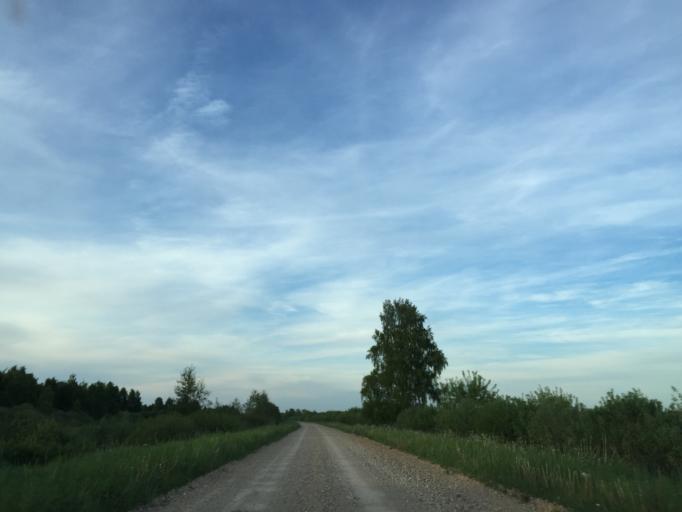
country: LV
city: Tireli
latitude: 56.7395
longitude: 23.5156
